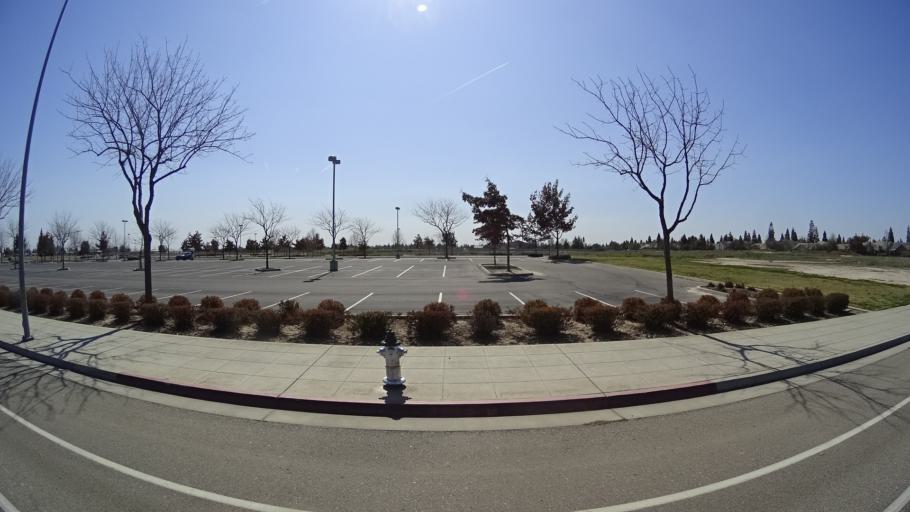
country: US
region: California
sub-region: Fresno County
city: Clovis
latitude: 36.8885
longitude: -119.7370
